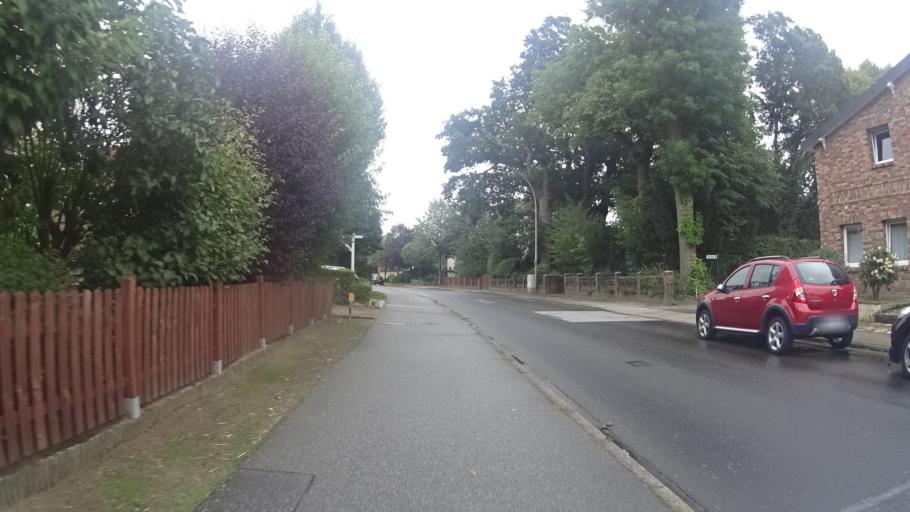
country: DE
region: Schleswig-Holstein
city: Kolln-Reisiek
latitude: 53.7565
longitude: 9.6926
